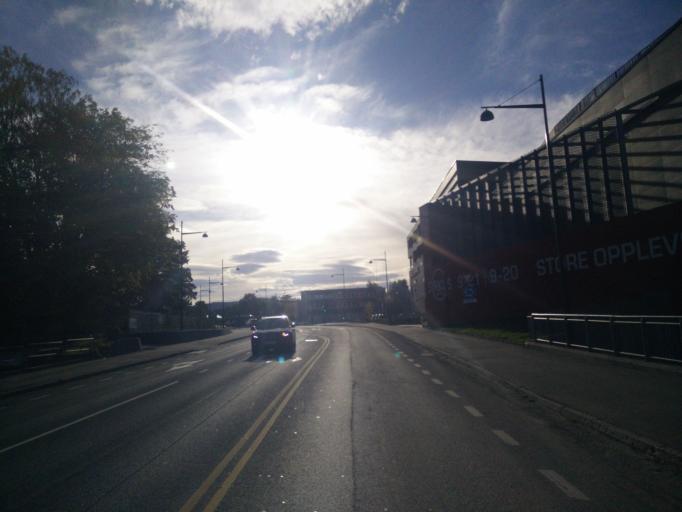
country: NO
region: Sor-Trondelag
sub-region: Trondheim
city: Trondheim
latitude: 63.4367
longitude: 10.4556
